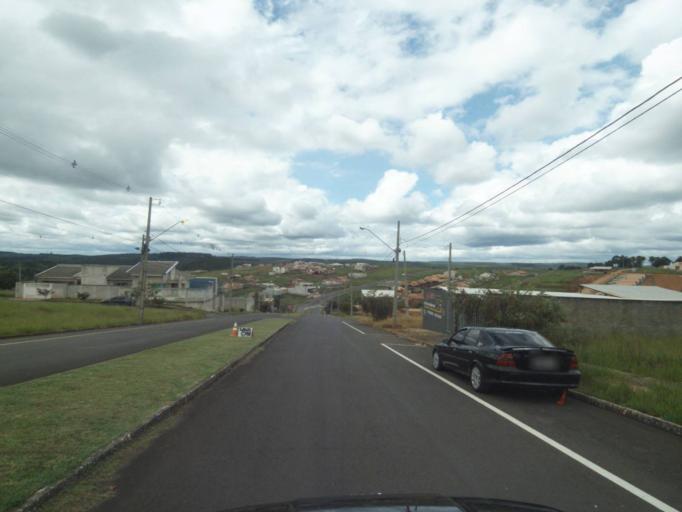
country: BR
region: Parana
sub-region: Telemaco Borba
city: Telemaco Borba
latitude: -24.3163
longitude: -50.6411
